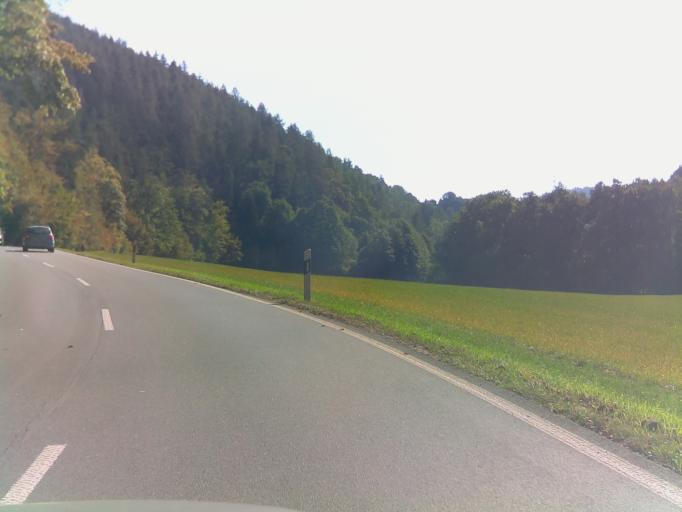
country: DE
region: Thuringia
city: Leutenberg
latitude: 50.5768
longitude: 11.4420
